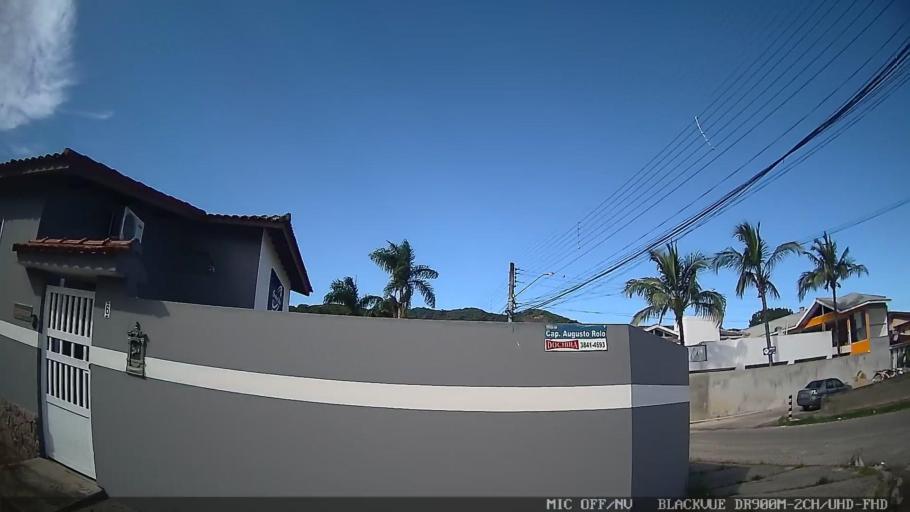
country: BR
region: Sao Paulo
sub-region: Iguape
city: Iguape
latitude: -24.7015
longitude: -47.5607
